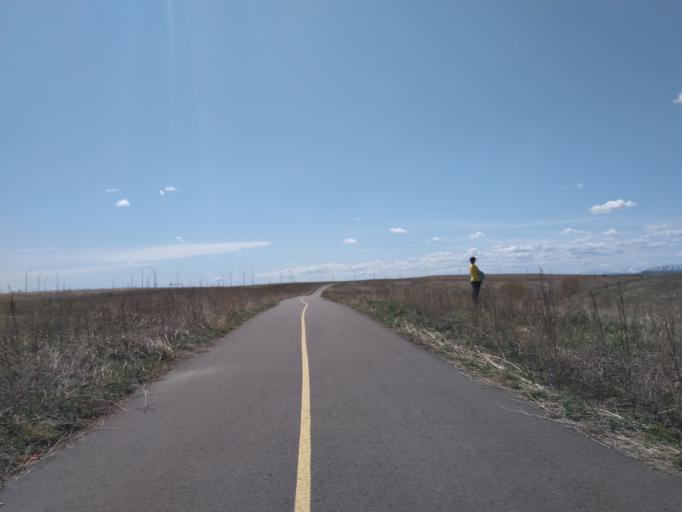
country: CA
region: Alberta
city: Chestermere
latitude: 51.0195
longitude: -113.9247
